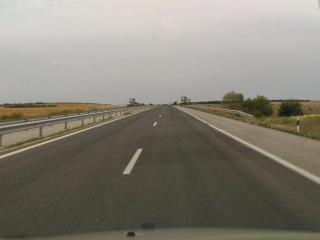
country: BG
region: Stara Zagora
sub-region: Obshtina Nikolaevo
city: Elkhovo
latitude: 42.2998
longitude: 25.4949
